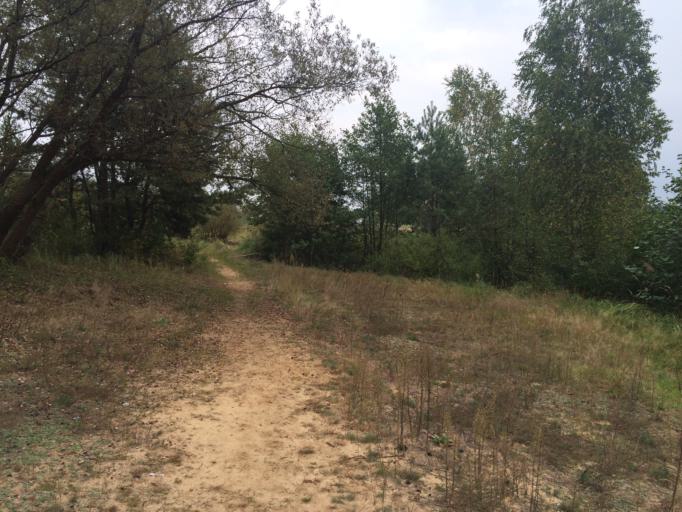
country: PL
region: Swietokrzyskie
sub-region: Powiat starachowicki
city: Starachowice
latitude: 51.0281
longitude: 21.0425
